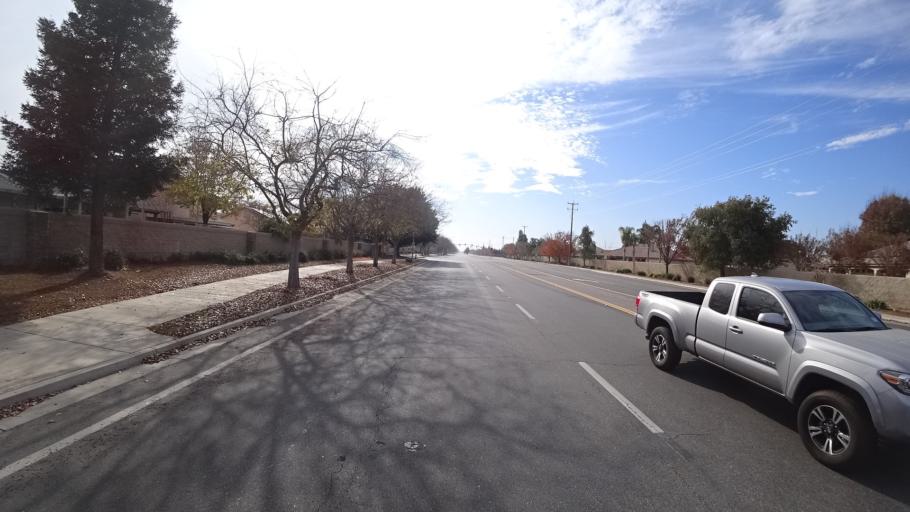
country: US
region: California
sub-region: Kern County
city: Rosedale
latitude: 35.4148
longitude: -119.1277
